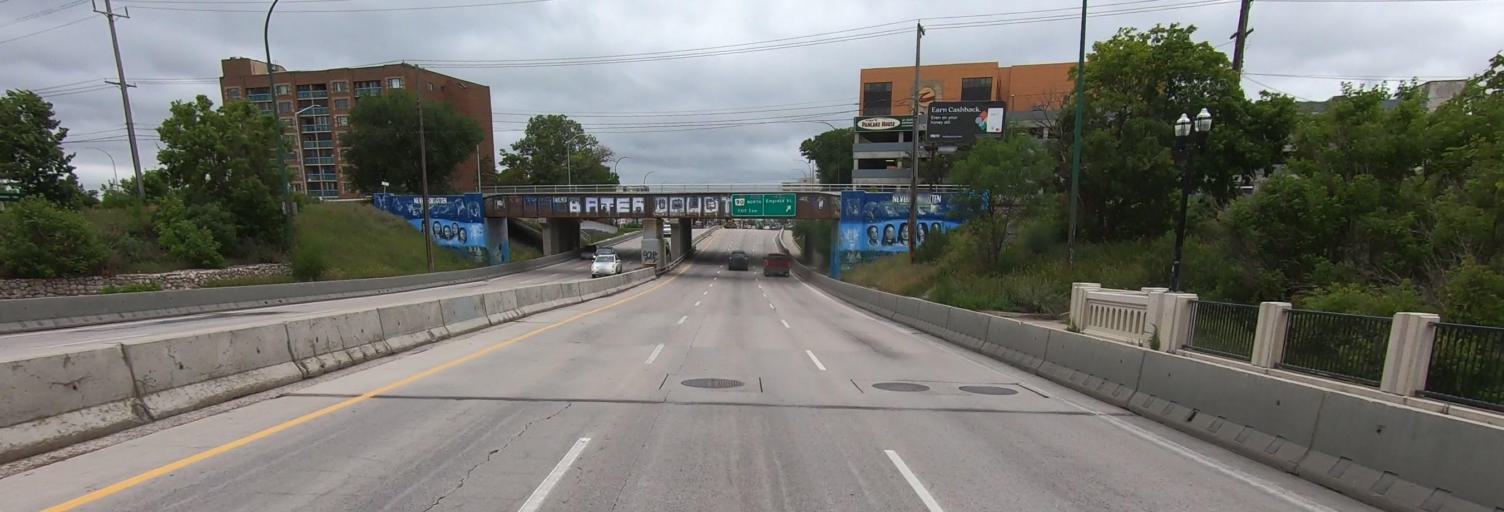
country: CA
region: Manitoba
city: Winnipeg
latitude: 49.8817
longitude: -97.1937
